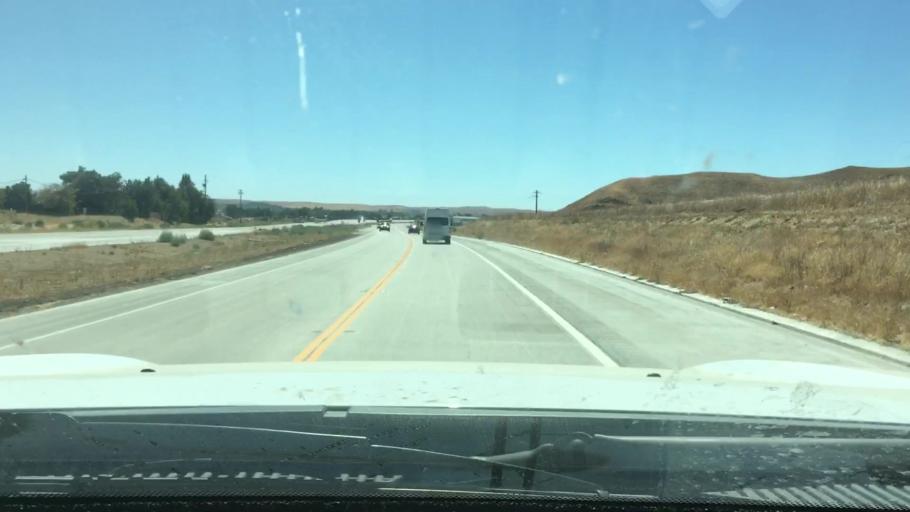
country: US
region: California
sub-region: San Luis Obispo County
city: Shandon
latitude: 35.6697
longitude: -120.3575
